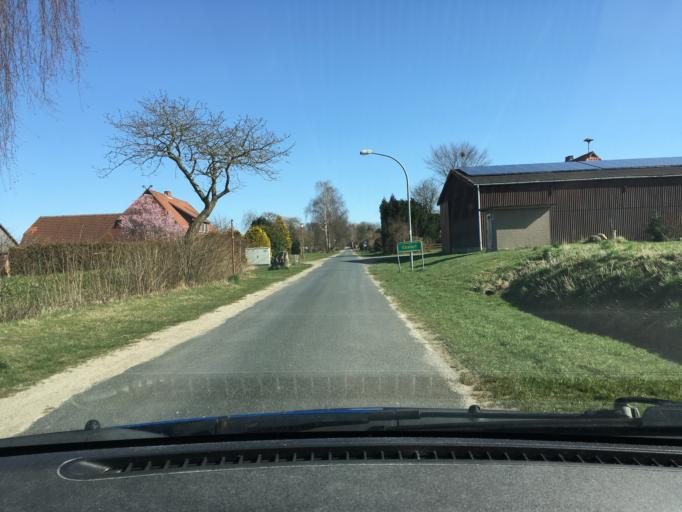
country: DE
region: Lower Saxony
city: Ebstorf
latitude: 53.0253
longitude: 10.4375
